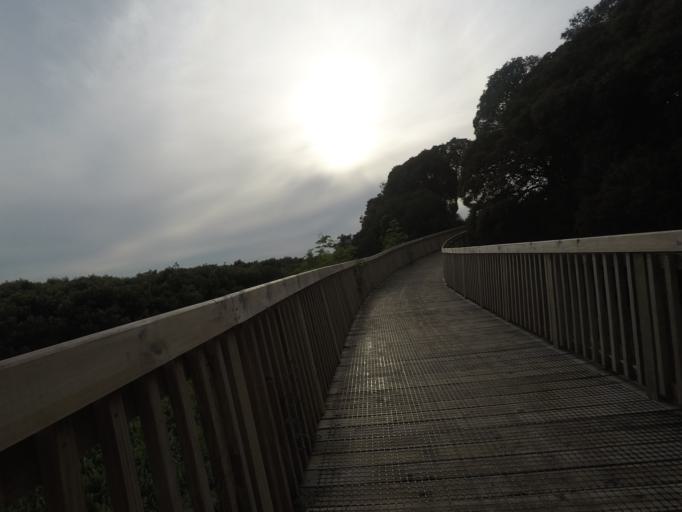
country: NZ
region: Auckland
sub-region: Auckland
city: Mangere
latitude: -36.9482
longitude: 174.8034
